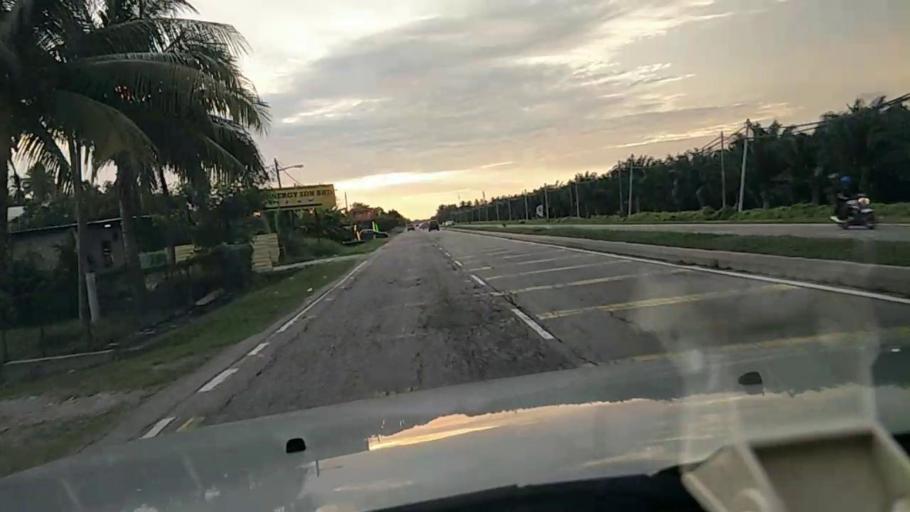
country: MY
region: Perak
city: Kampong Dungun
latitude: 3.1422
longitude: 101.3605
